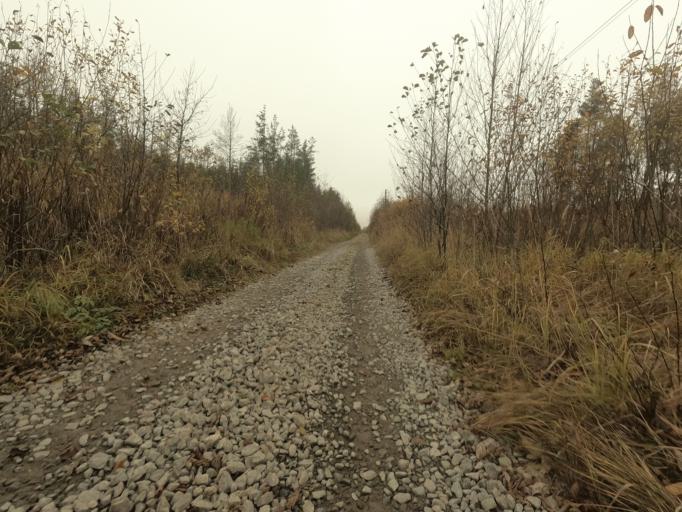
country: RU
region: Leningrad
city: Pavlovo
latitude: 59.7675
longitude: 30.9399
